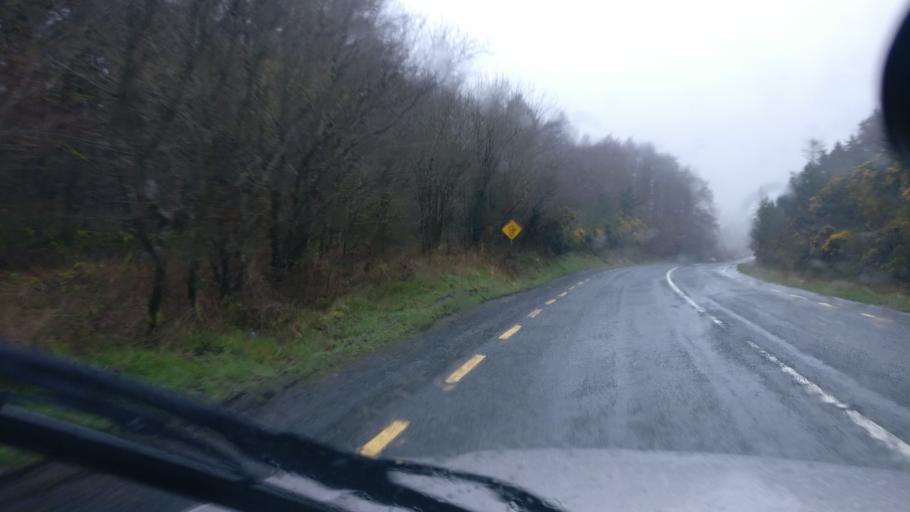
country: IE
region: Connaught
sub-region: County Galway
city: Loughrea
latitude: 53.1439
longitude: -8.4709
